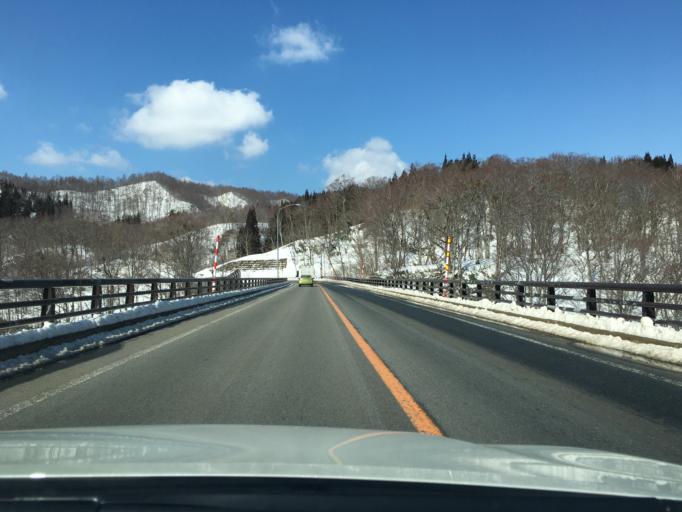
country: JP
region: Yamagata
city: Tsuruoka
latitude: 38.5782
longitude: 139.9432
